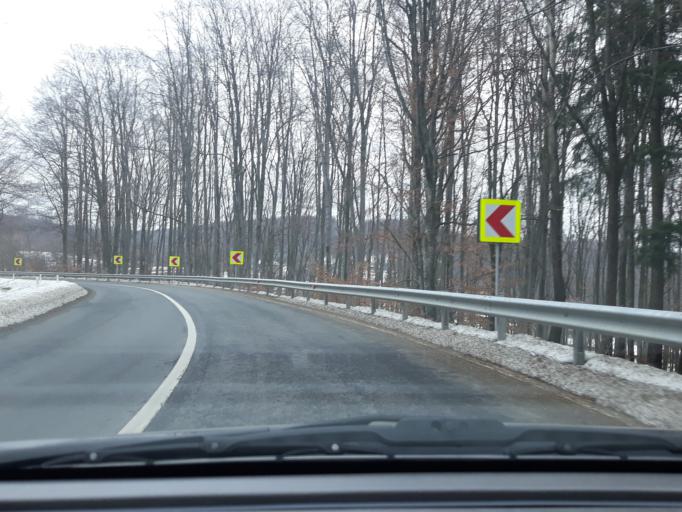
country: RO
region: Bihor
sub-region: Comuna Sinteu
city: Sinteu
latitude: 47.1213
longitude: 22.4489
